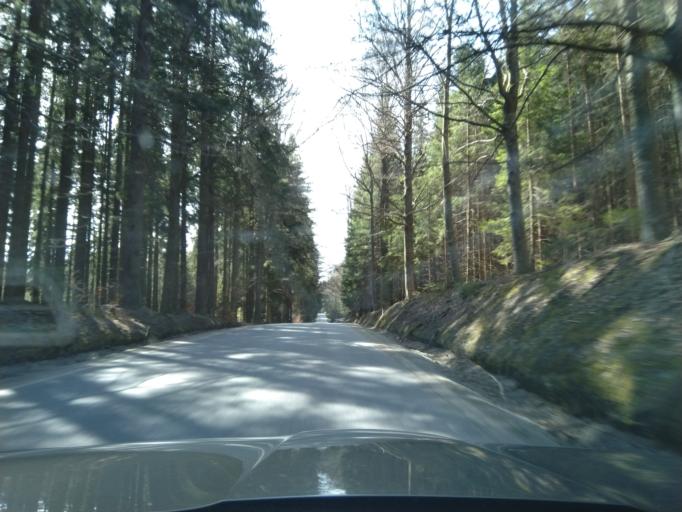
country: CZ
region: Jihocesky
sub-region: Okres Prachatice
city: Stachy
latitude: 49.0624
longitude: 13.6559
